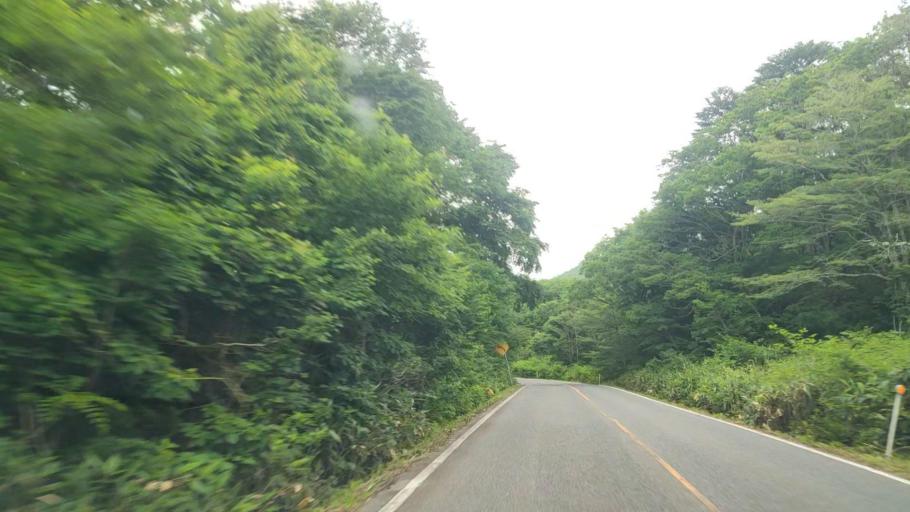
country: JP
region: Tottori
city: Kurayoshi
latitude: 35.3443
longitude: 133.5836
